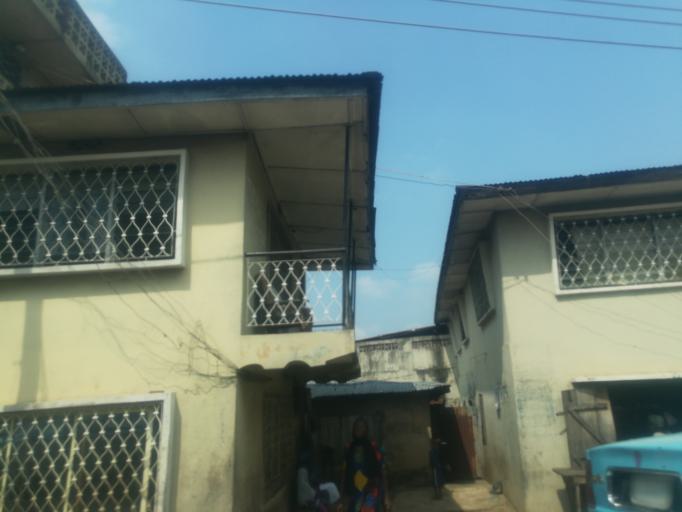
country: NG
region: Oyo
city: Ibadan
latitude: 7.3928
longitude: 3.9075
